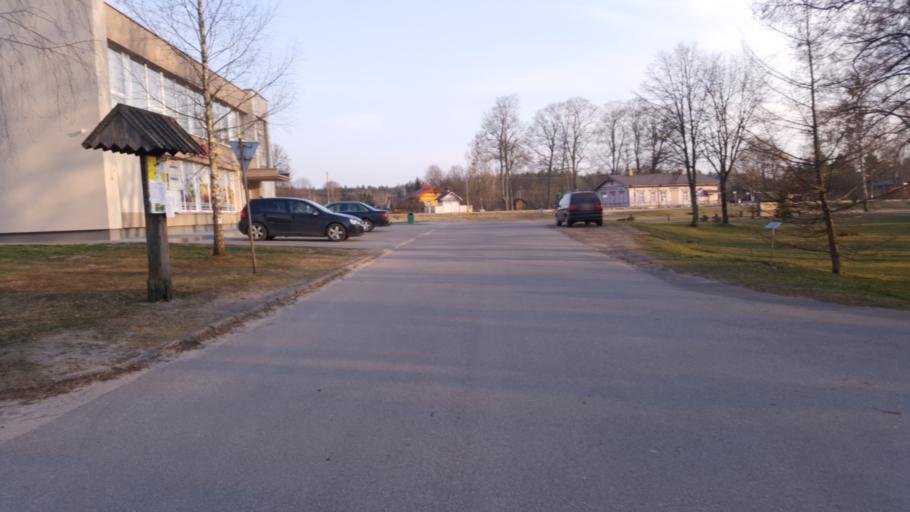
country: LT
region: Alytaus apskritis
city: Varena
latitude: 54.0538
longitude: 24.4077
